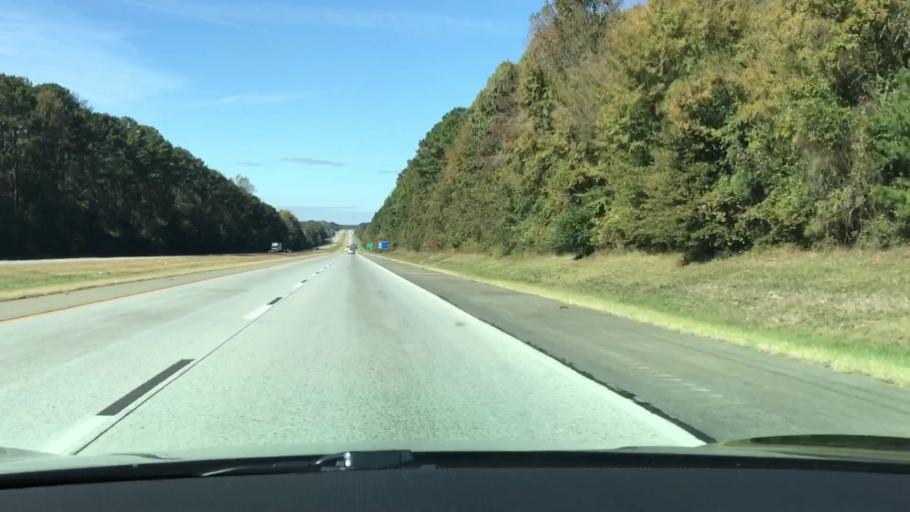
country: US
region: Georgia
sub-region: Putnam County
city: Jefferson
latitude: 33.5438
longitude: -83.3286
